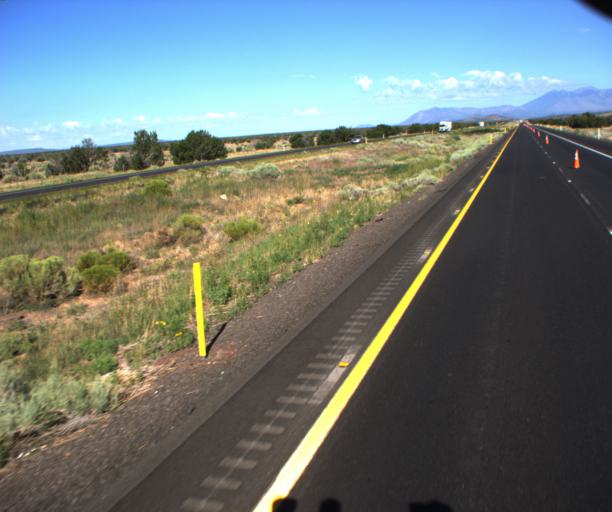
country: US
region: Arizona
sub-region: Coconino County
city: Flagstaff
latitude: 35.1660
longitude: -111.3171
